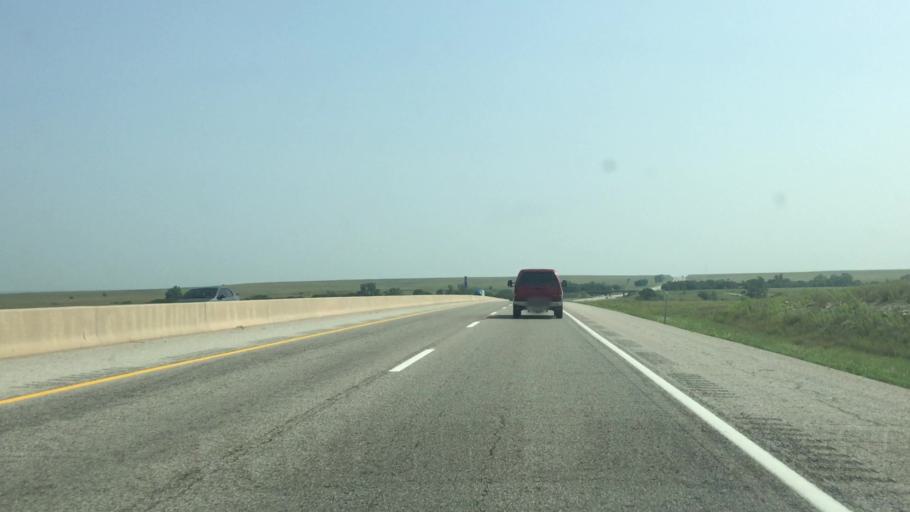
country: US
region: Kansas
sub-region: Lyon County
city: Emporia
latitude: 38.3064
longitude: -96.3441
